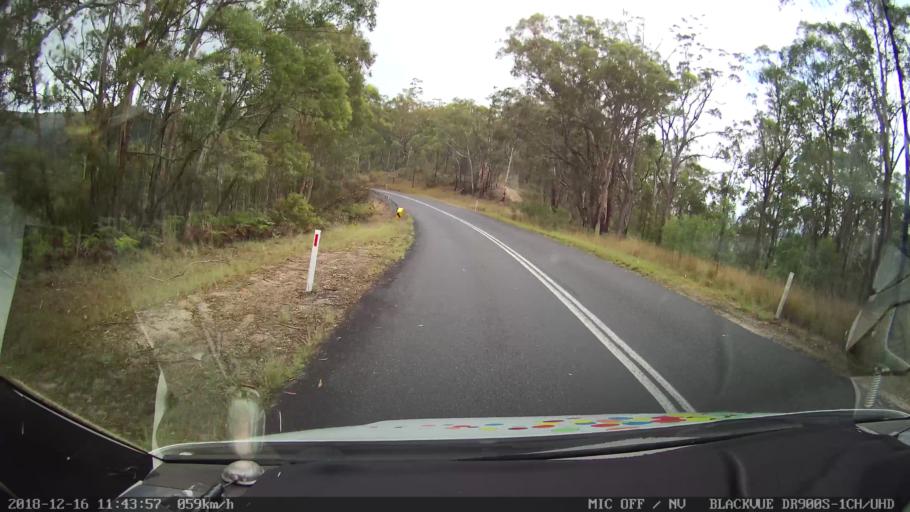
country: AU
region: New South Wales
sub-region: Tenterfield Municipality
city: Carrolls Creek
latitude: -28.9424
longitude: 152.2205
